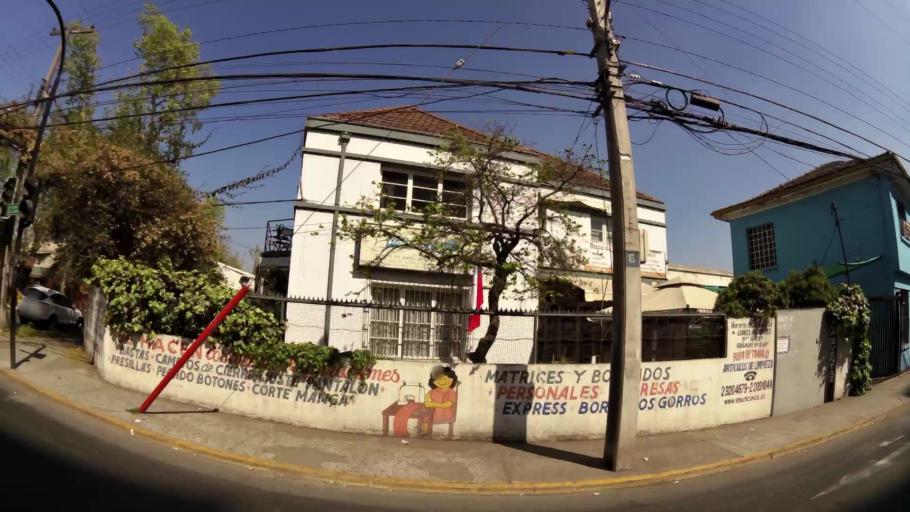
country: CL
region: Santiago Metropolitan
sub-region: Provincia de Santiago
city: Santiago
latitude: -33.4552
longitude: -70.6250
